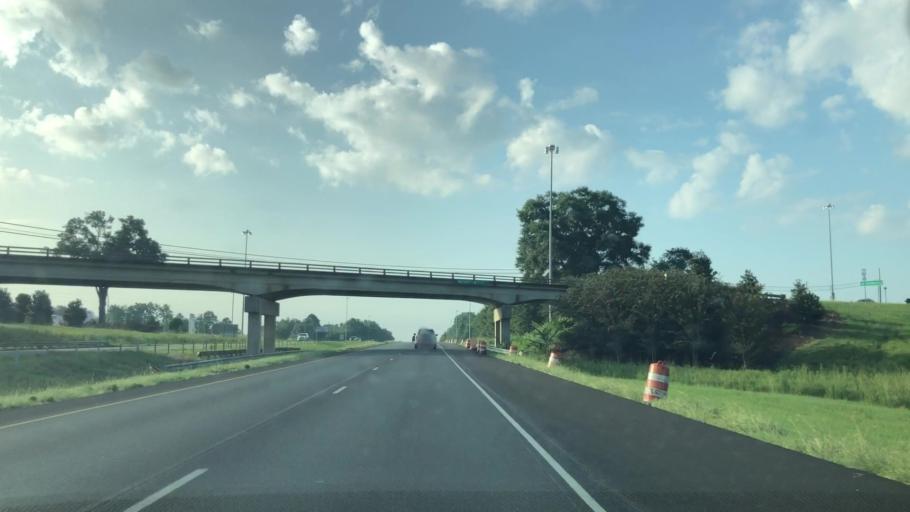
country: US
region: Alabama
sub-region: Chilton County
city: Clanton
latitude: 32.8887
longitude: -86.6246
